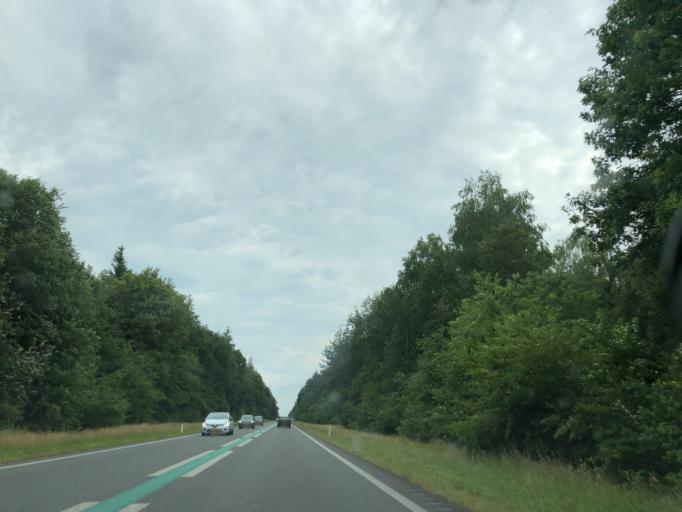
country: NL
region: Drenthe
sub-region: Gemeente Borger-Odoorn
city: Borger
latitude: 52.9627
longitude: 6.7799
